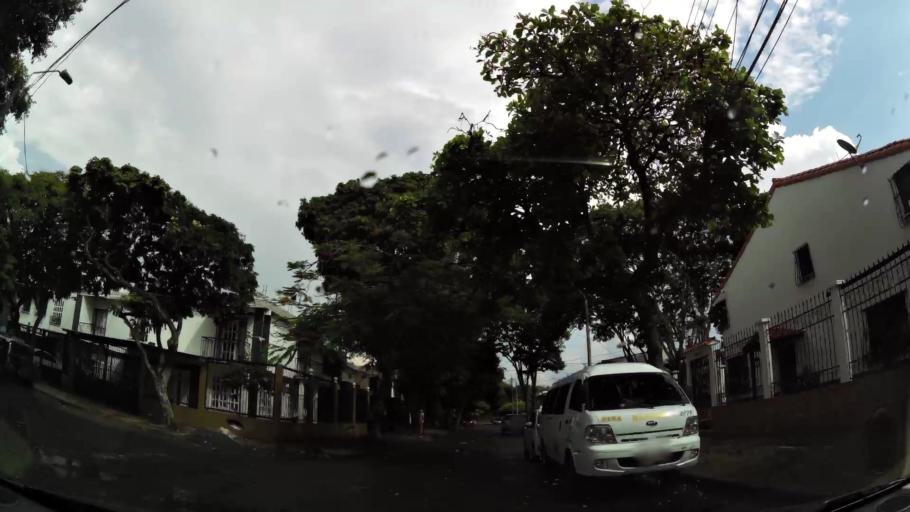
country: CO
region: Valle del Cauca
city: Cali
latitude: 3.4795
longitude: -76.5132
